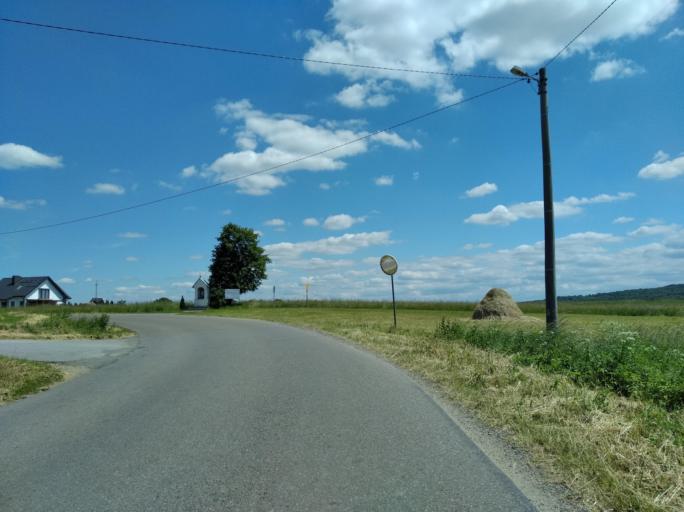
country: PL
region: Subcarpathian Voivodeship
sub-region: Powiat jasielski
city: Osiek Jasielski
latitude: 49.6632
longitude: 21.5425
